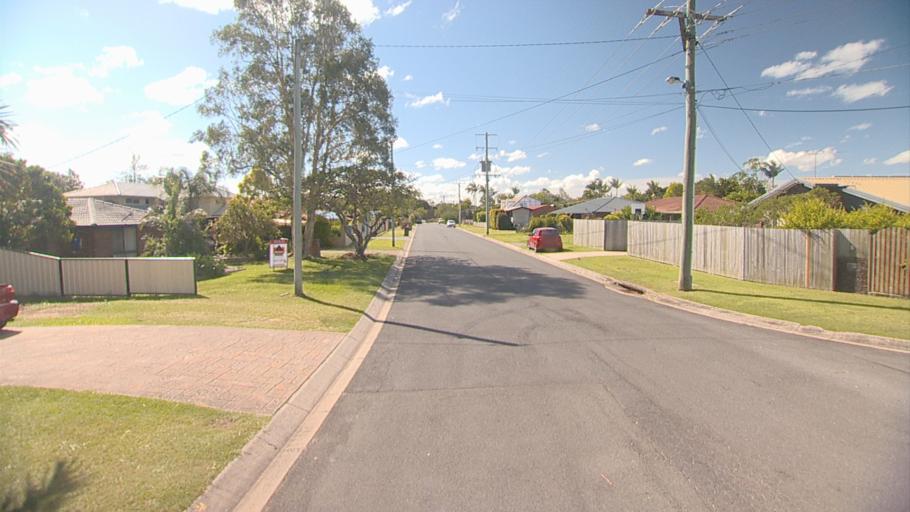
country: AU
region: Queensland
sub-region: Logan
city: Waterford West
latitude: -27.6810
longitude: 153.1433
